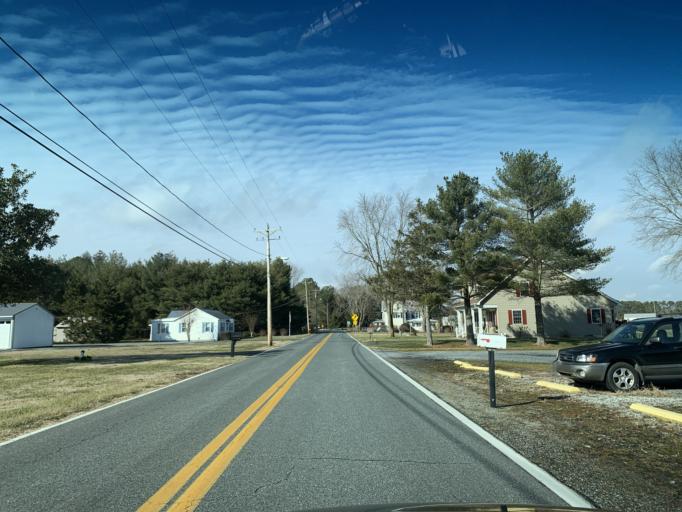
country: US
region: Delaware
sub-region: Sussex County
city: Selbyville
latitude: 38.4474
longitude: -75.1925
